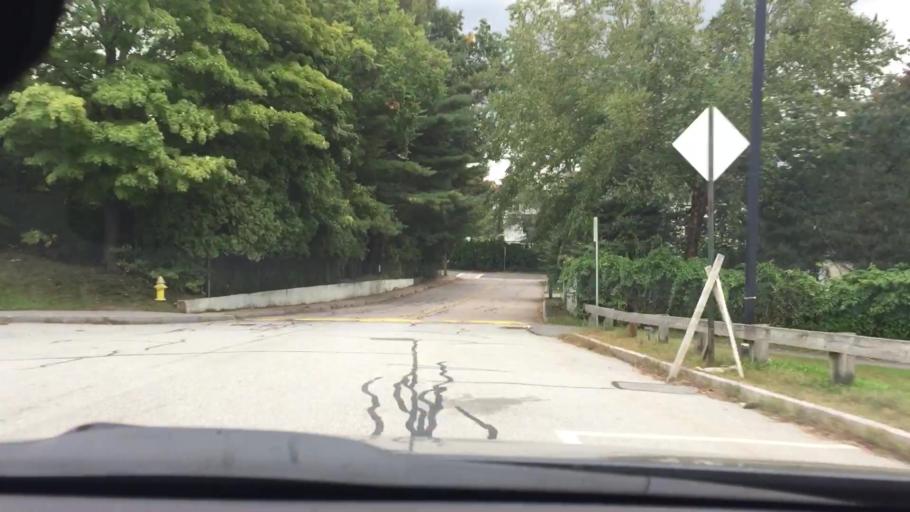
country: US
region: Massachusetts
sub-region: Norfolk County
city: Needham
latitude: 42.2855
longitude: -71.2320
